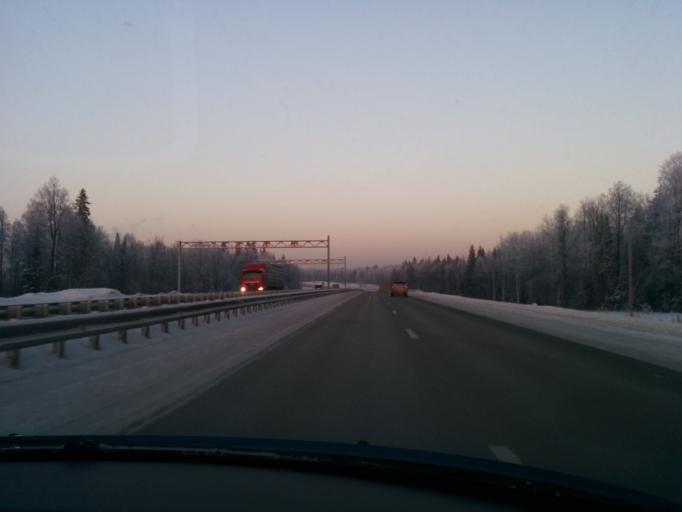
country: RU
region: Perm
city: Ferma
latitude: 58.0262
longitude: 56.4268
